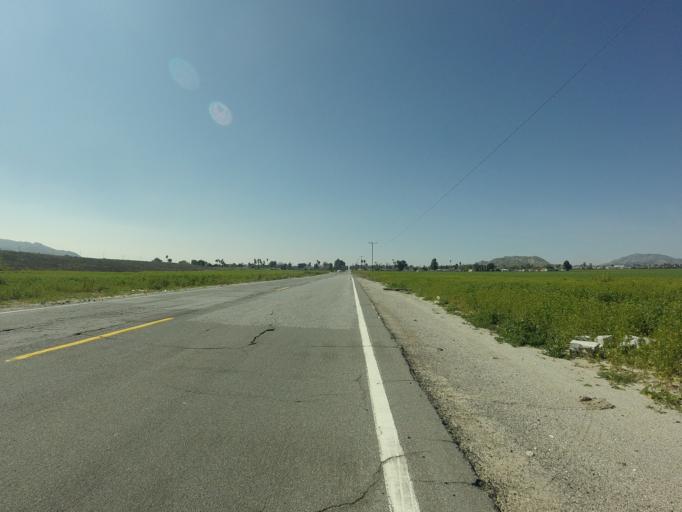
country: US
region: California
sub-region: Riverside County
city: Lakeview
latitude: 33.9175
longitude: -117.1457
